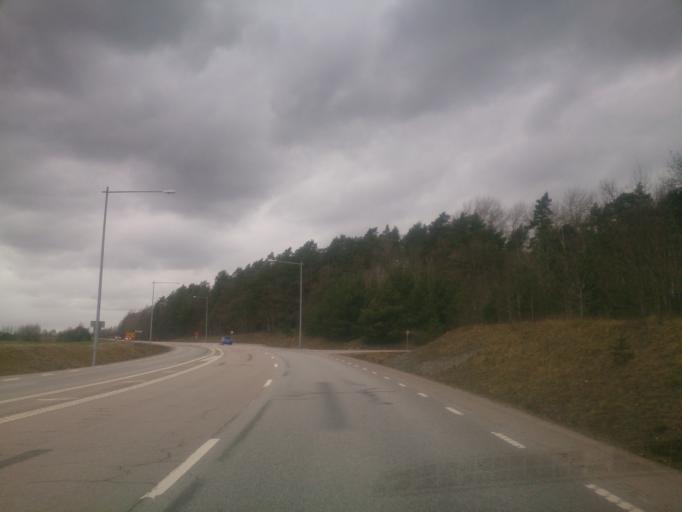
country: SE
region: OEstergoetland
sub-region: Norrkopings Kommun
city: Svartinge
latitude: 58.5703
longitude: 16.0748
